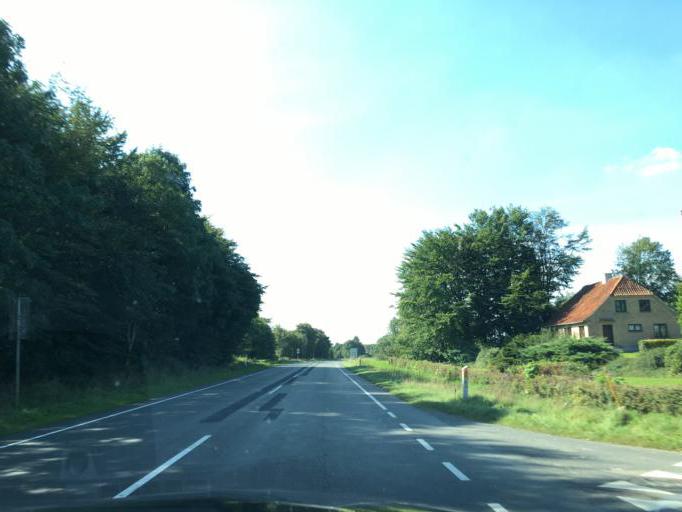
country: DK
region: South Denmark
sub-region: Vejen Kommune
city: Vejen
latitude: 55.4699
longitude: 9.1896
